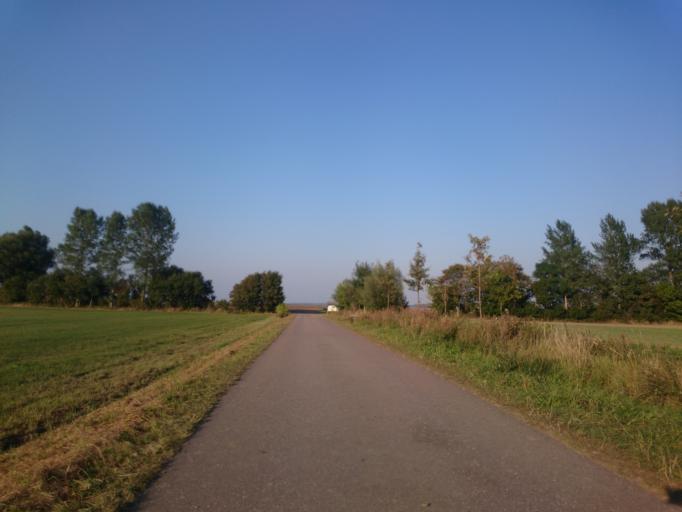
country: DE
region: Mecklenburg-Vorpommern
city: Velgast
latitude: 54.3420
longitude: 12.8235
